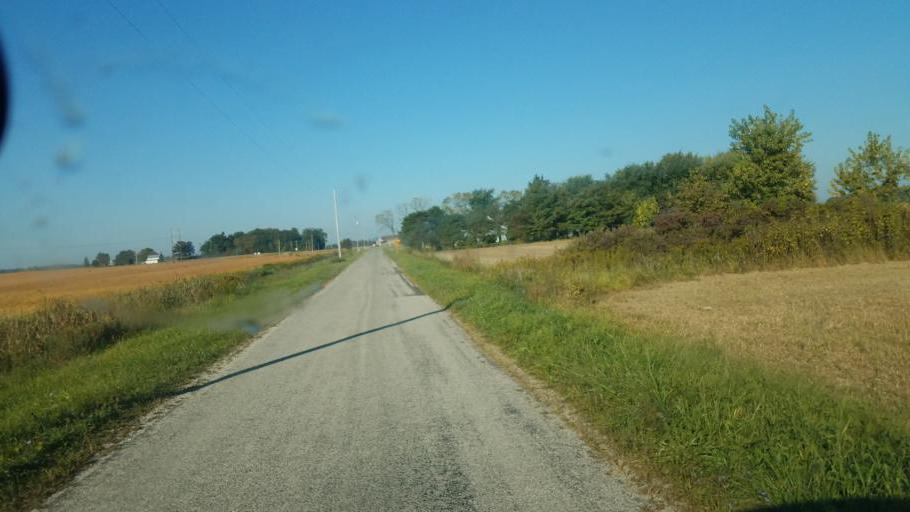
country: US
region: Ohio
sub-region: Marion County
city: Prospect
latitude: 40.5303
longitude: -83.2608
